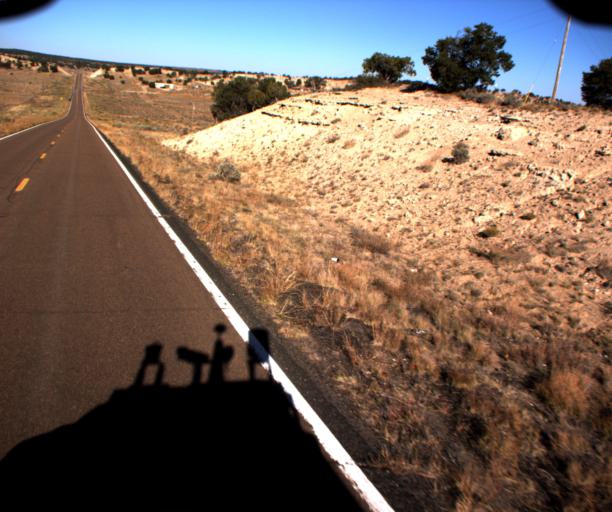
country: US
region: Arizona
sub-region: Navajo County
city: First Mesa
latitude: 35.7603
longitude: -109.9674
